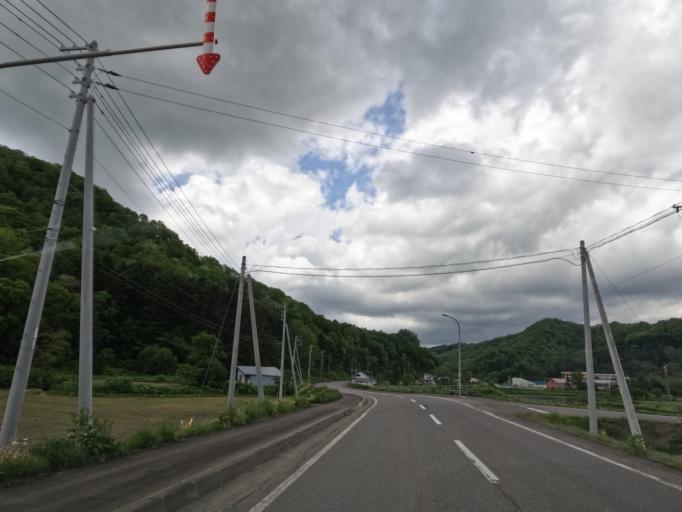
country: JP
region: Hokkaido
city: Takikawa
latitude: 43.5902
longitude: 141.7321
